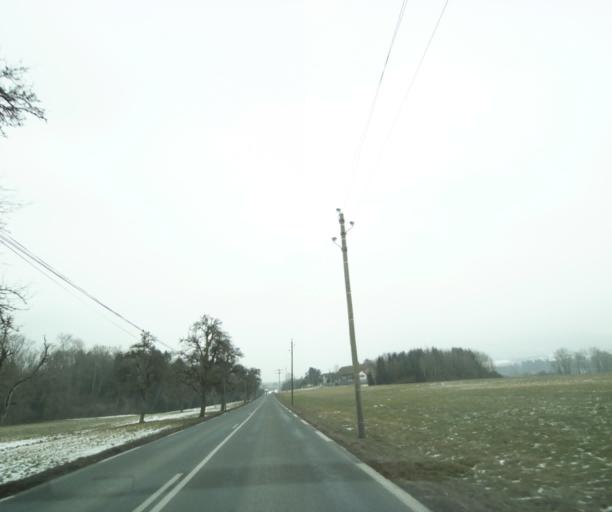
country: FR
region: Rhone-Alpes
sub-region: Departement de la Haute-Savoie
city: Contamine-sur-Arve
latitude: 46.1293
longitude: 6.3131
